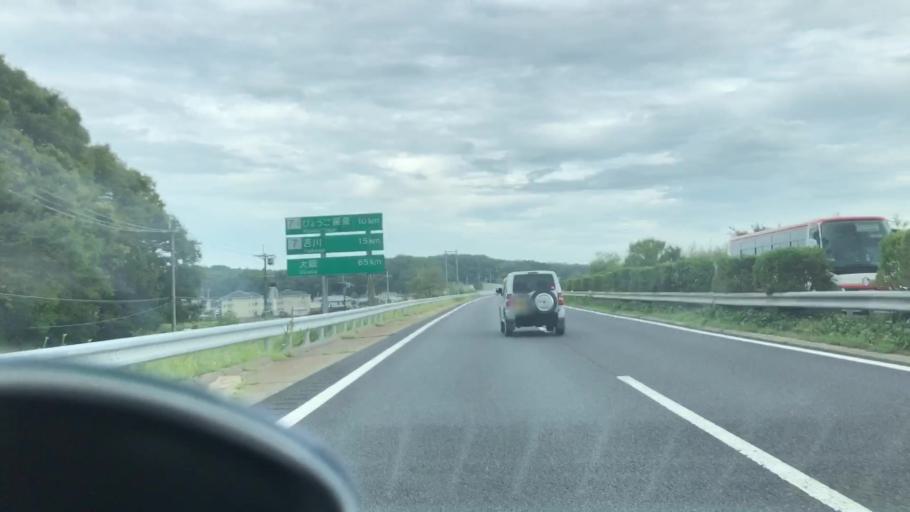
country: JP
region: Hyogo
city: Yashiro
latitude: 34.9287
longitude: 134.9816
